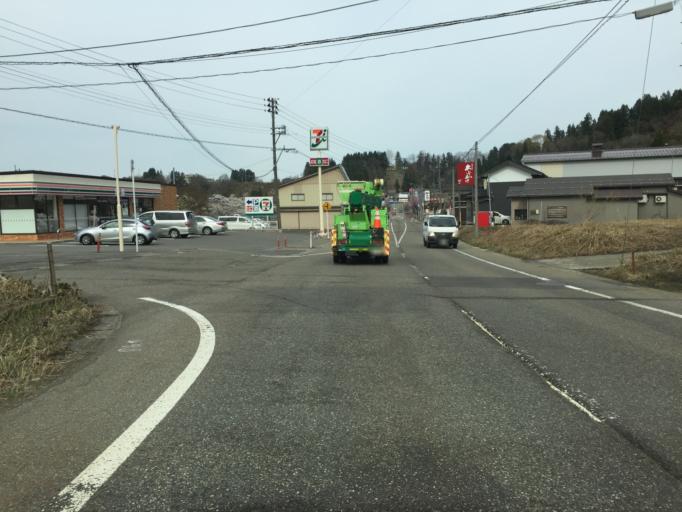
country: JP
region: Niigata
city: Tochio-honcho
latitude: 37.4658
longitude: 138.9882
